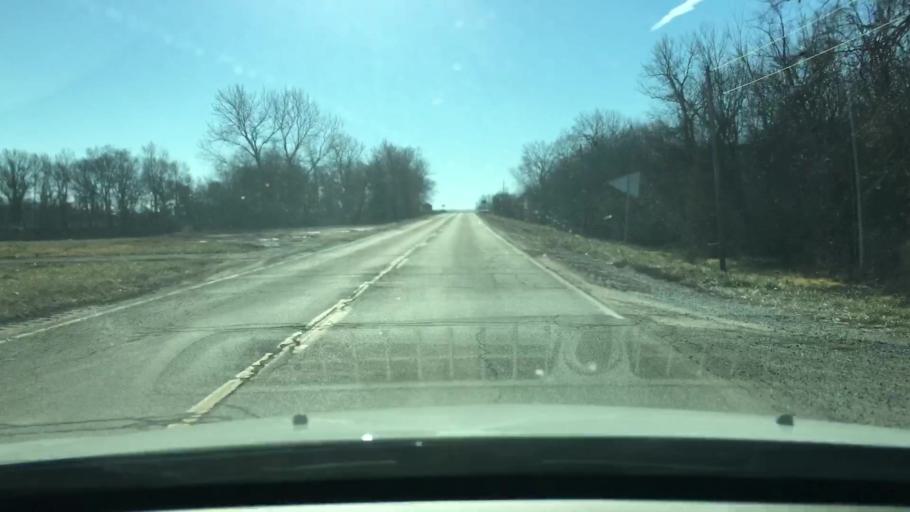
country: US
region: Illinois
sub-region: Mason County
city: Havana
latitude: 40.2752
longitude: -90.1747
